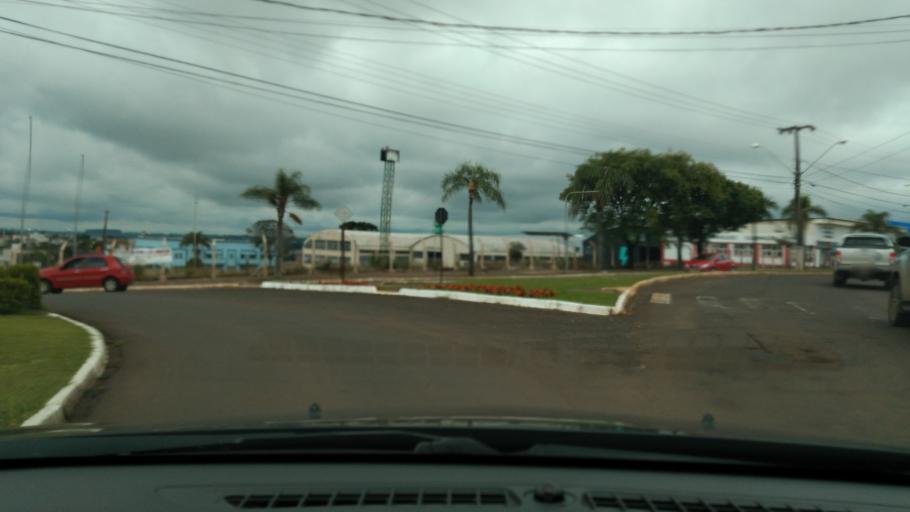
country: BR
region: Parana
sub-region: Guarapuava
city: Guarapuava
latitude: -25.3825
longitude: -51.4679
